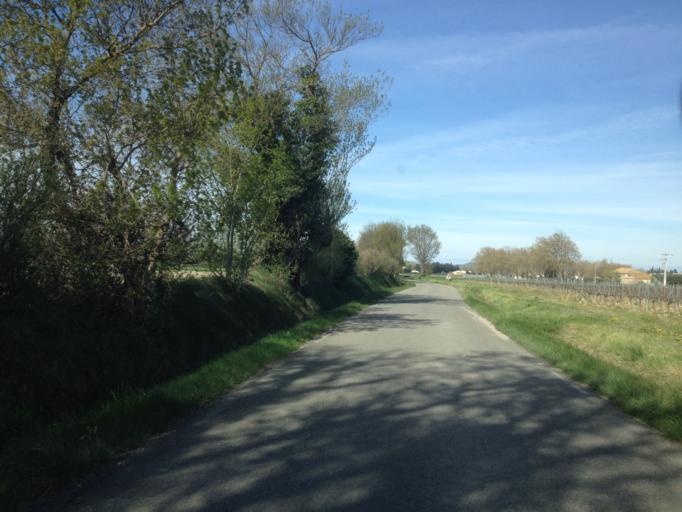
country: FR
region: Provence-Alpes-Cote d'Azur
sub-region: Departement du Vaucluse
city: Caderousse
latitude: 44.0982
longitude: 4.7695
